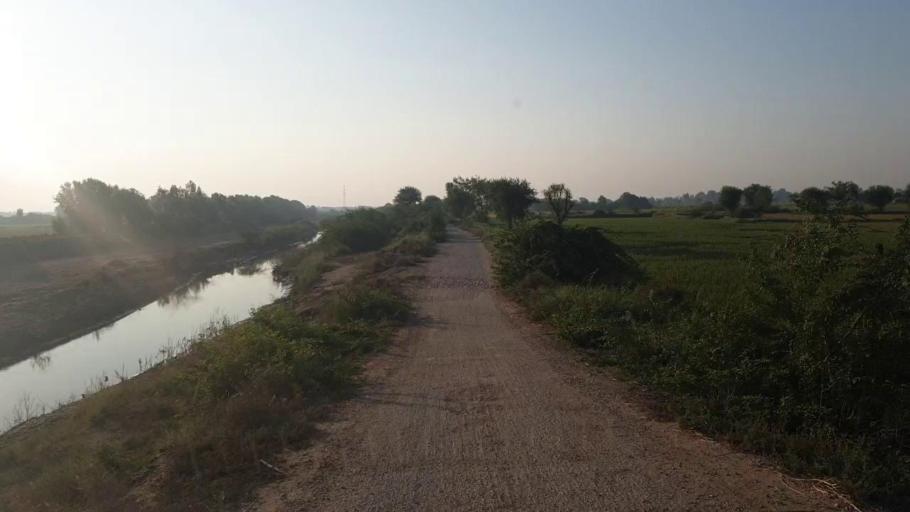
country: PK
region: Sindh
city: Badin
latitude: 24.6597
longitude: 68.7867
